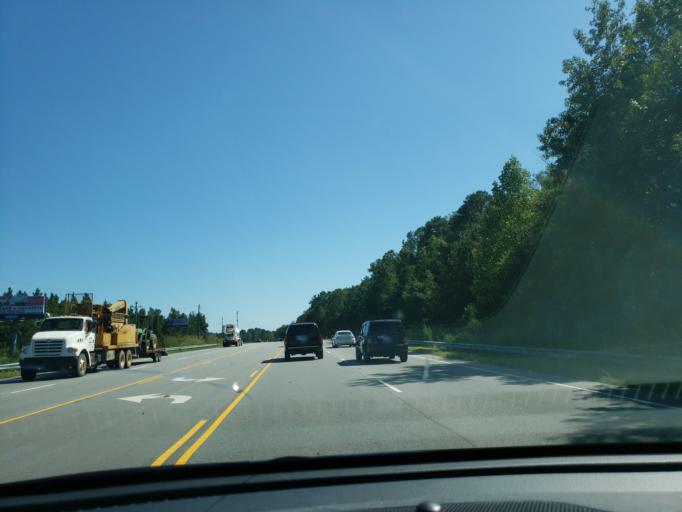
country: US
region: North Carolina
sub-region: Lee County
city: Broadway
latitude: 35.3567
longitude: -79.1097
